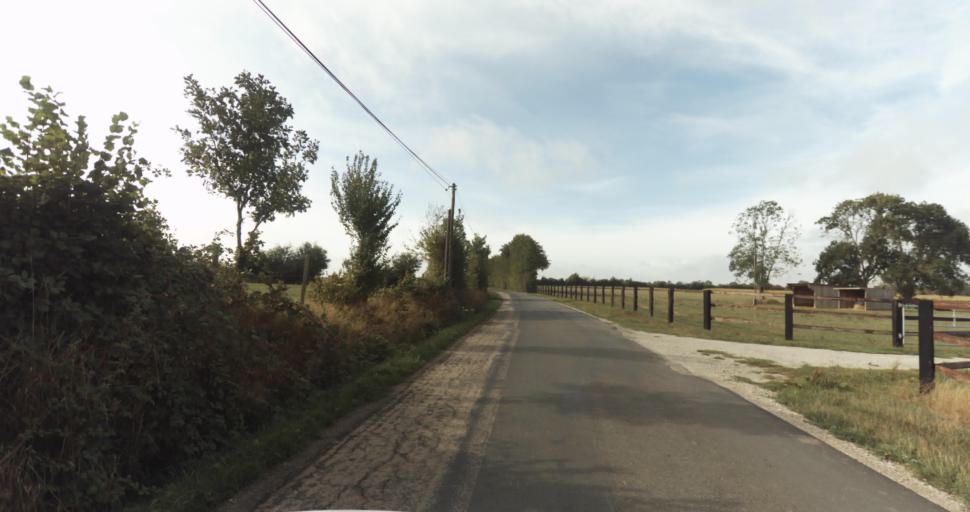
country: FR
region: Lower Normandy
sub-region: Departement de l'Orne
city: Gace
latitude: 48.9093
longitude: 0.3417
